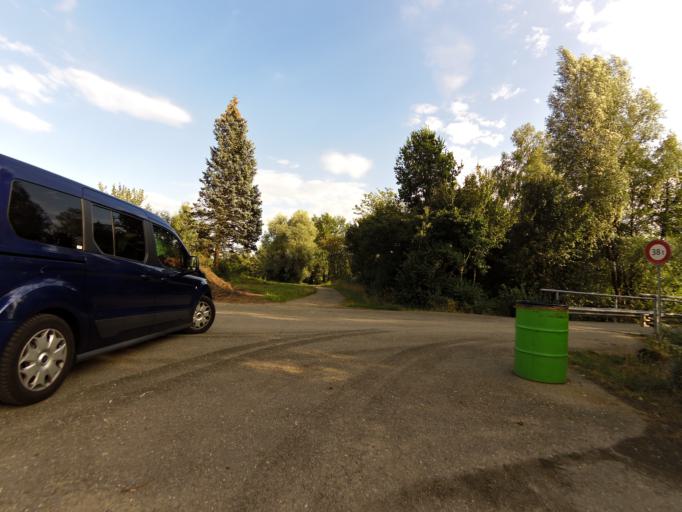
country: CH
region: Zurich
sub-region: Bezirk Buelach
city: Bachenbulach
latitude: 47.4787
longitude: 8.5451
